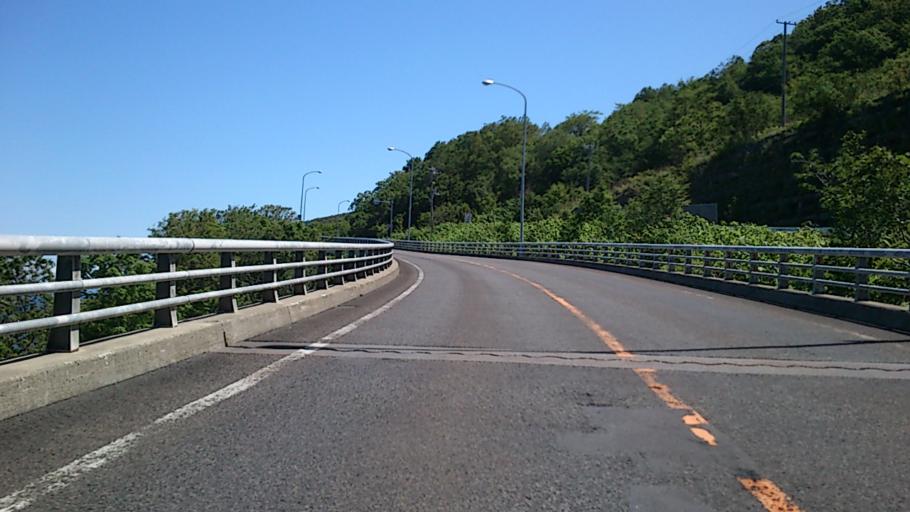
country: JP
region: Hokkaido
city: Rumoi
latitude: 43.8143
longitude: 141.4134
